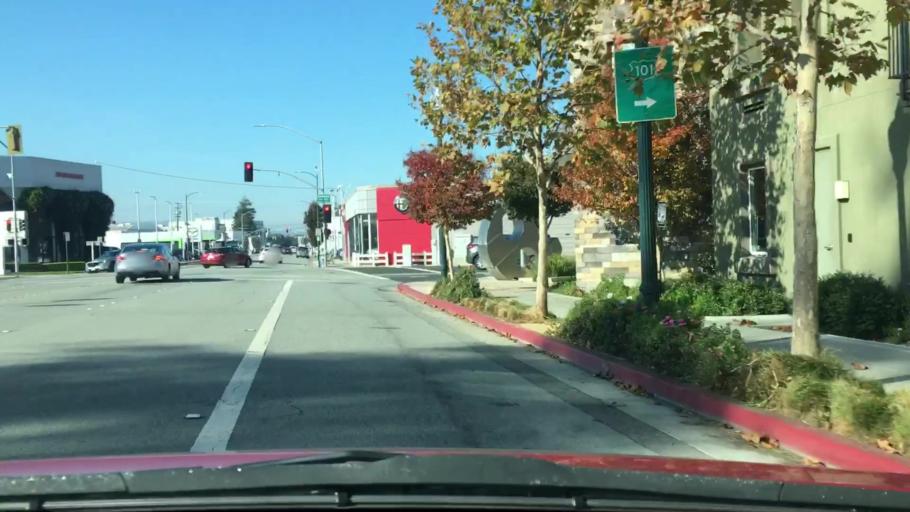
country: US
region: California
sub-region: San Mateo County
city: San Mateo
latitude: 37.5769
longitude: -122.3389
